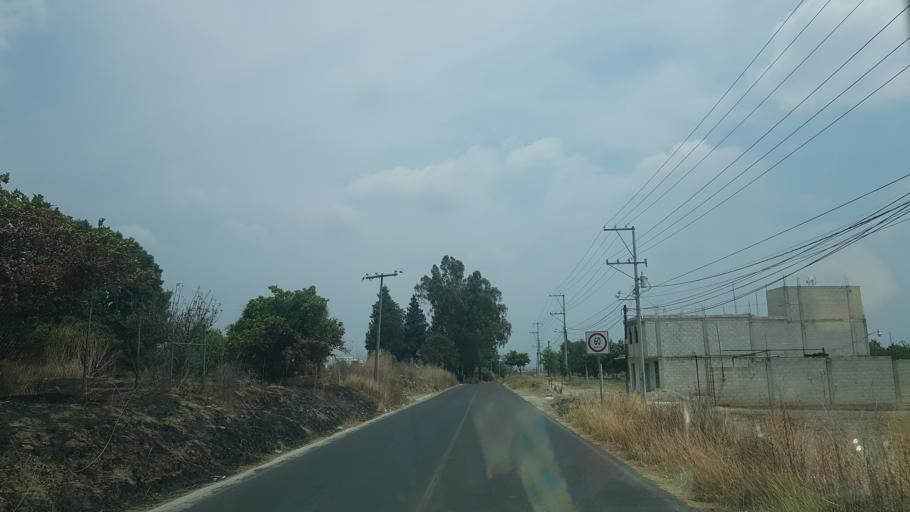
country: MX
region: Puebla
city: Huejotzingo
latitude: 19.1399
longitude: -98.4125
